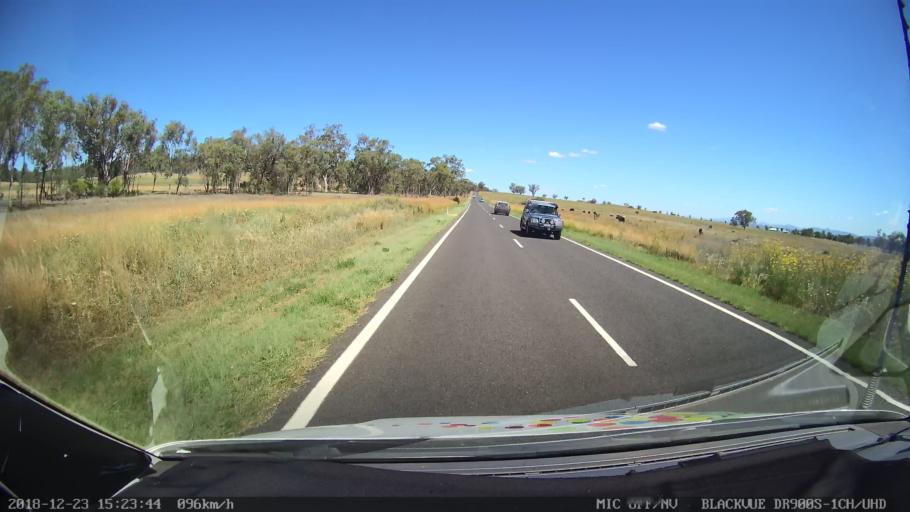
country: AU
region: New South Wales
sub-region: Tamworth Municipality
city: Manilla
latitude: -30.8837
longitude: 150.8170
